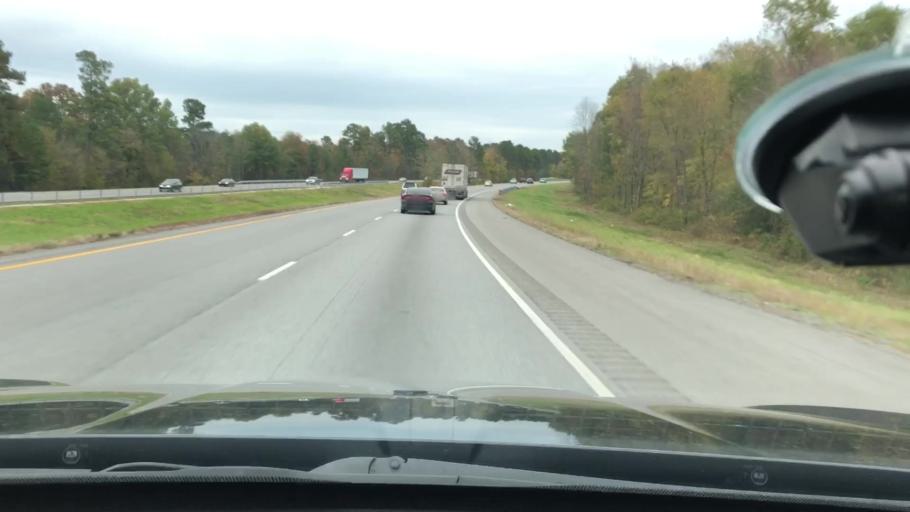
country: US
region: Arkansas
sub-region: Hempstead County
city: Hope
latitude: 33.6196
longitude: -93.7888
